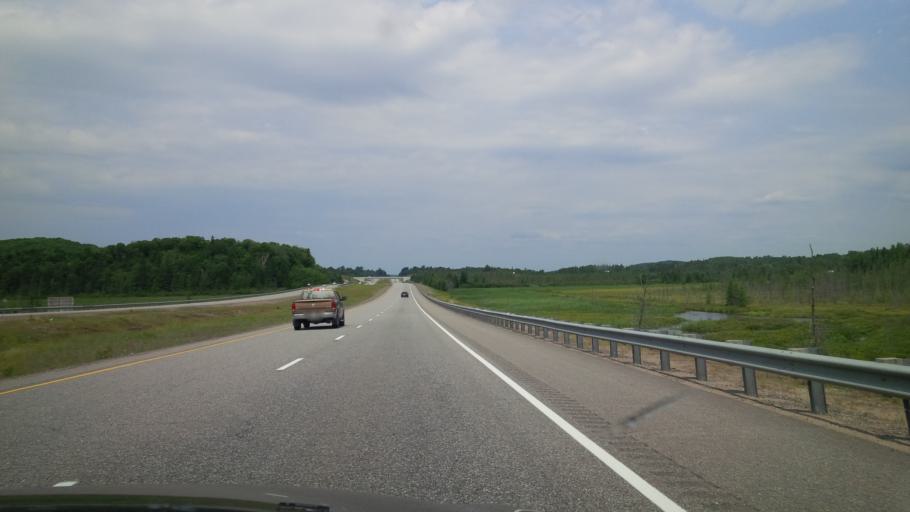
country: CA
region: Ontario
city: Huntsville
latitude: 45.5005
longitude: -79.2962
